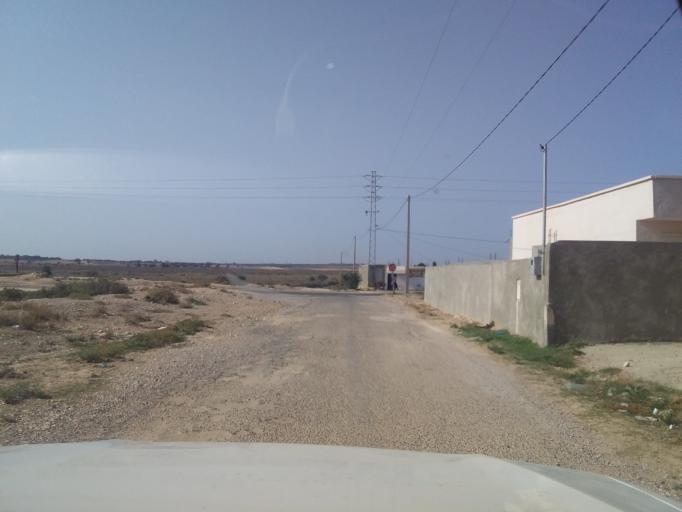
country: TN
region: Qabis
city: Gabes
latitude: 33.6414
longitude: 10.2951
